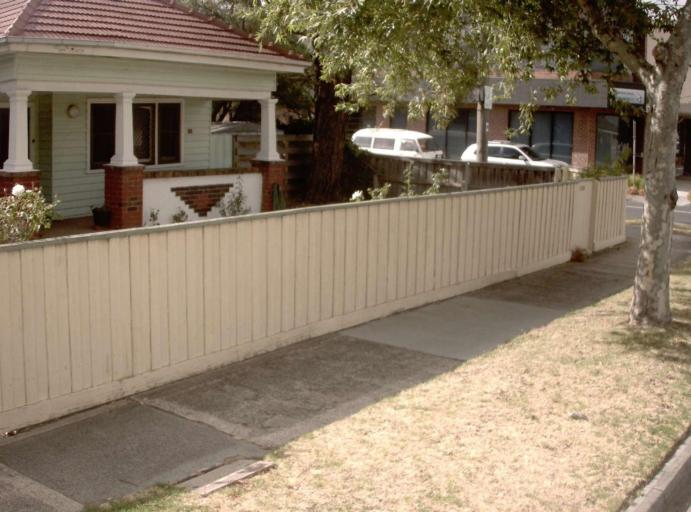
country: AU
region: Victoria
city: Clayton
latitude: -37.9048
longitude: 145.1048
